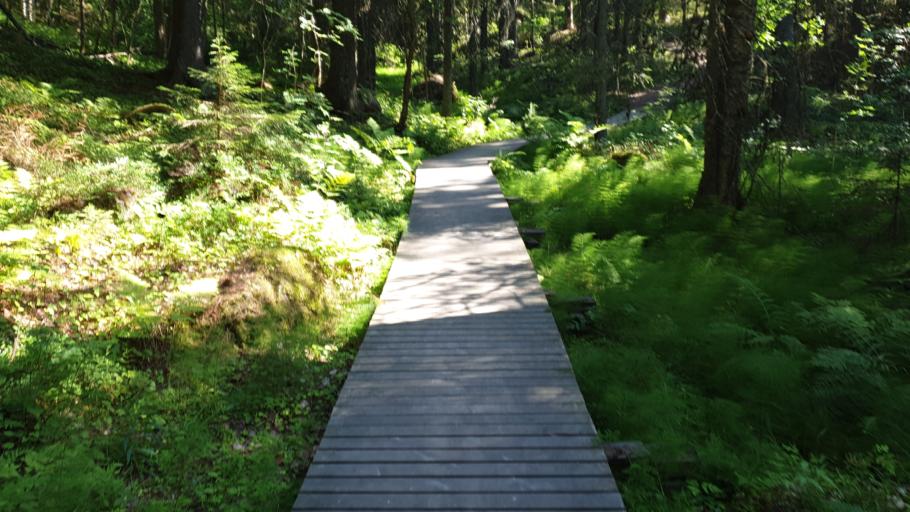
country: SE
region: Vaesternorrland
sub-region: OErnskoeldsviks Kommun
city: Husum
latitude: 63.4971
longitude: 18.9267
